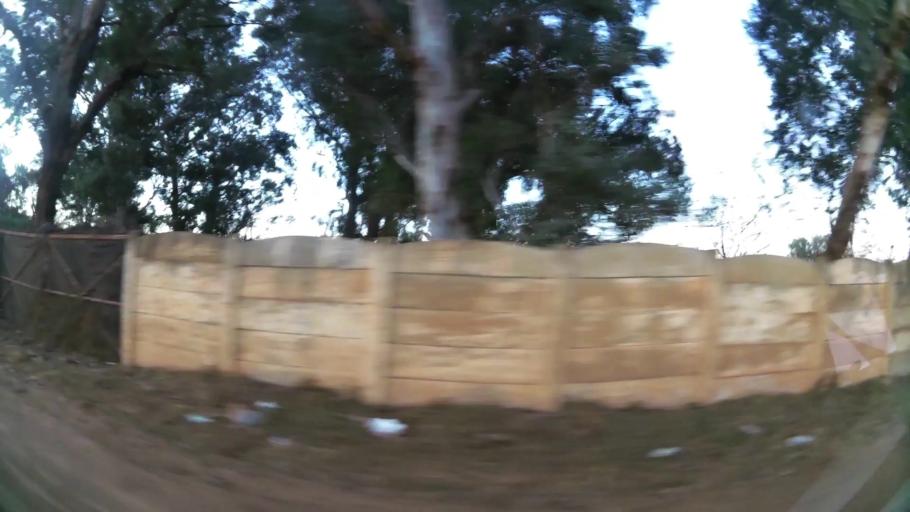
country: ZA
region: North-West
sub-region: Dr Kenneth Kaunda District Municipality
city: Potchefstroom
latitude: -26.7094
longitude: 27.1231
